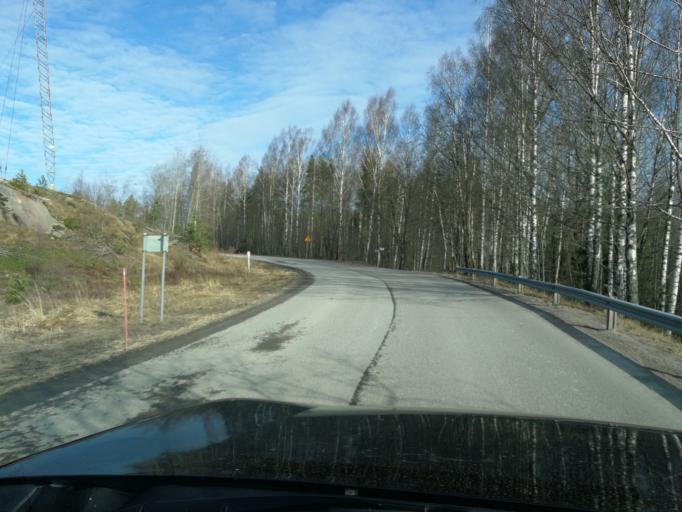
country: FI
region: Uusimaa
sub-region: Helsinki
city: Kirkkonummi
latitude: 60.0920
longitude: 24.3816
